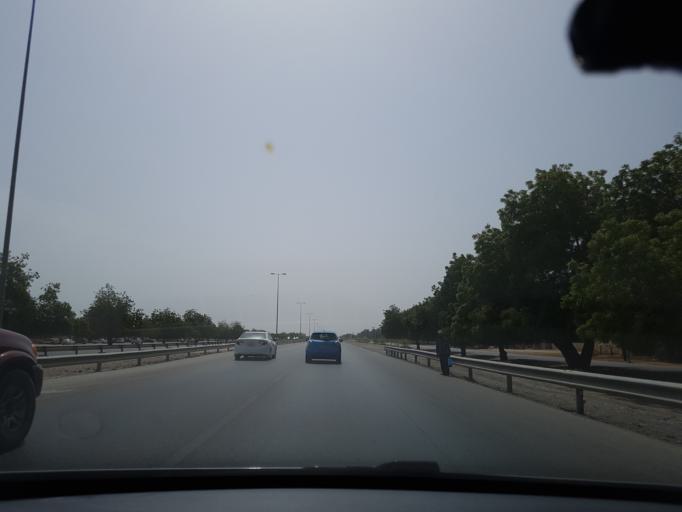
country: OM
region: Al Batinah
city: As Suwayq
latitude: 23.8374
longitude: 57.3830
